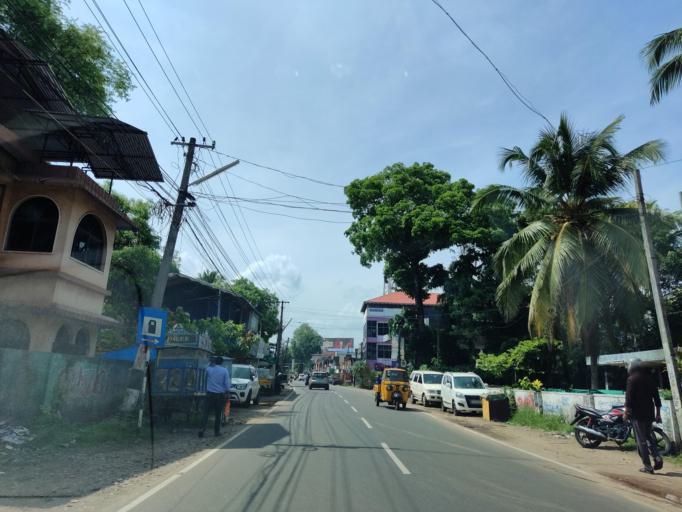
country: IN
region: Kerala
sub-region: Alappuzha
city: Mavelikara
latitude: 9.3102
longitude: 76.5342
